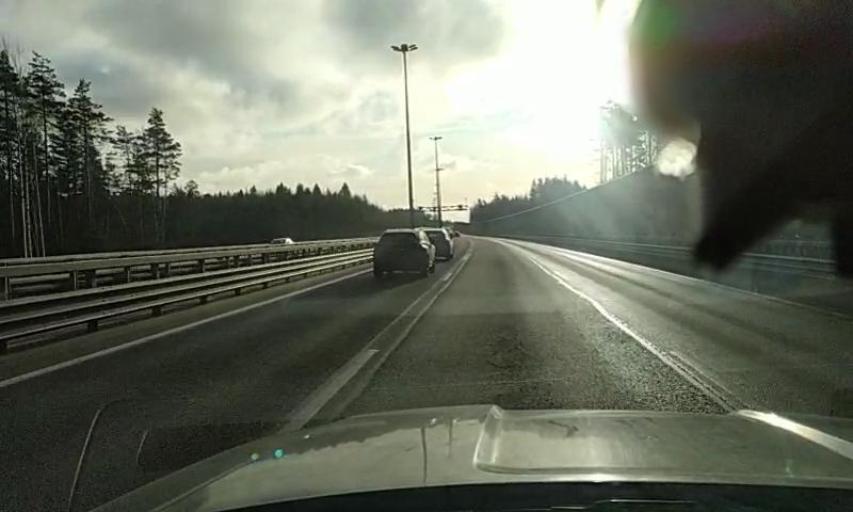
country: RU
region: St.-Petersburg
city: Beloostrov
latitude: 60.1197
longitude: 30.0731
